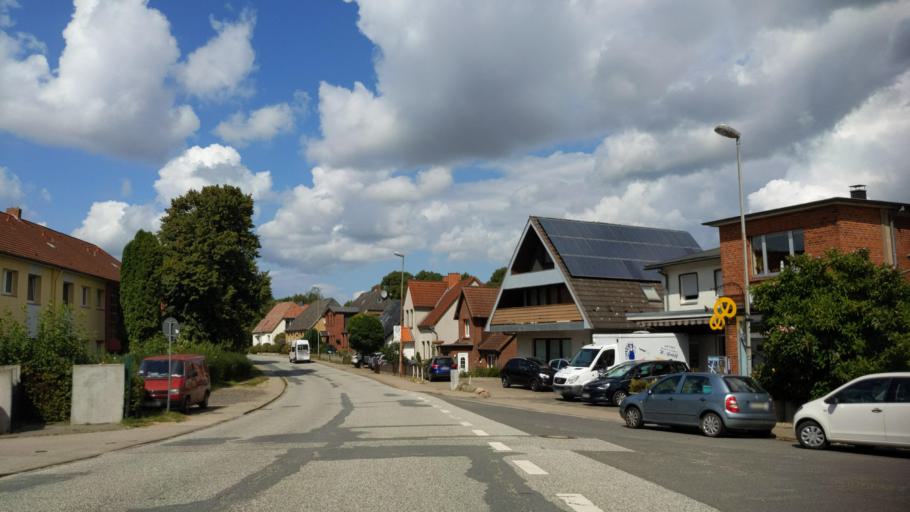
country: DE
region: Schleswig-Holstein
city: Reinfeld
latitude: 53.8291
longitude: 10.4778
